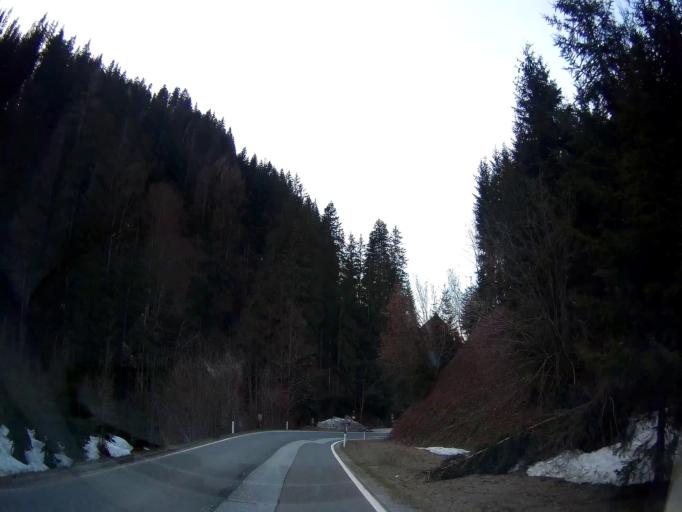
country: AT
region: Salzburg
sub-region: Politischer Bezirk Hallein
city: Abtenau
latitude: 47.5381
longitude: 13.4220
